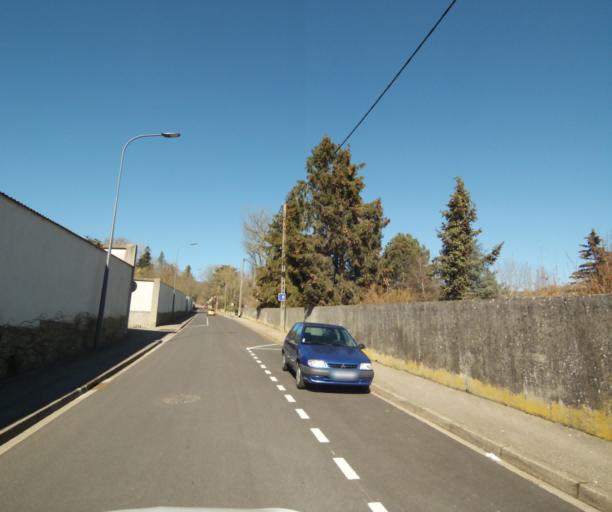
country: FR
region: Lorraine
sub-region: Departement de Meurthe-et-Moselle
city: Saint-Max
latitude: 48.7081
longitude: 6.2157
